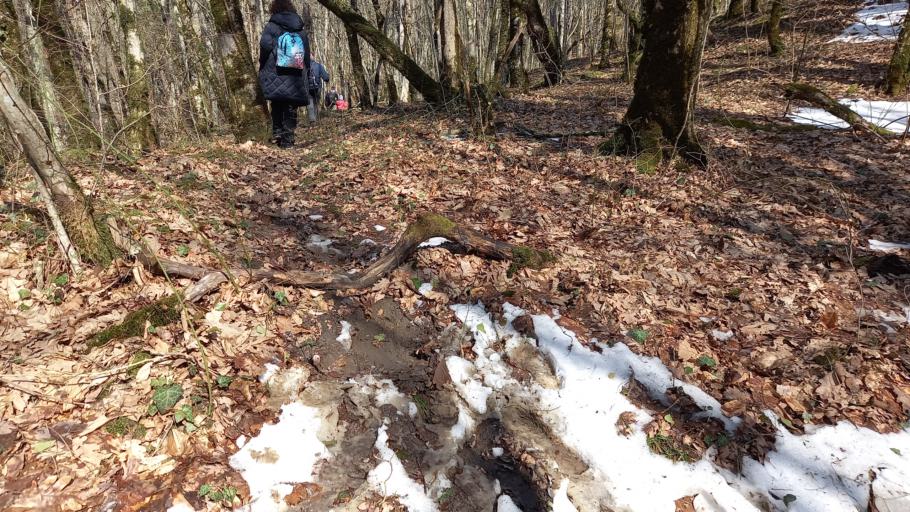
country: RU
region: Krasnodarskiy
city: Arkhipo-Osipovka
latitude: 44.3843
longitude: 38.6037
